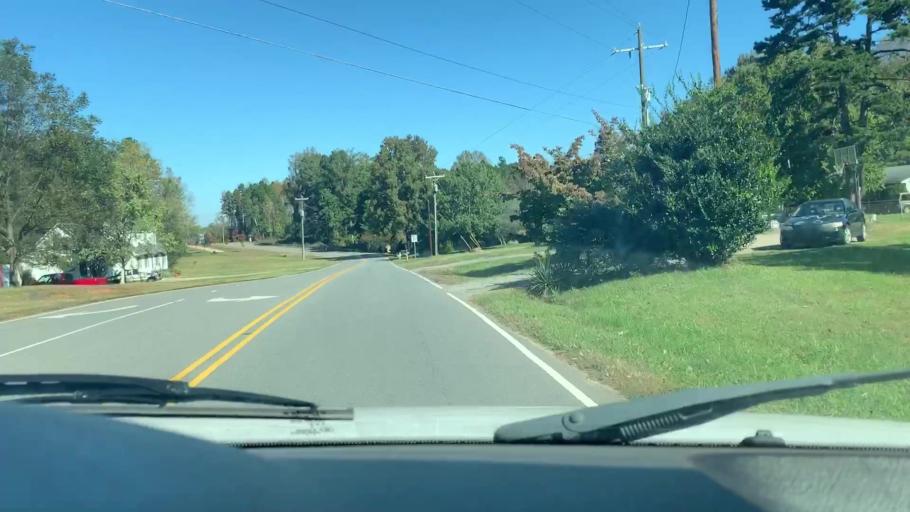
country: US
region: North Carolina
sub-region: Gaston County
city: Davidson
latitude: 35.4575
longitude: -80.8210
